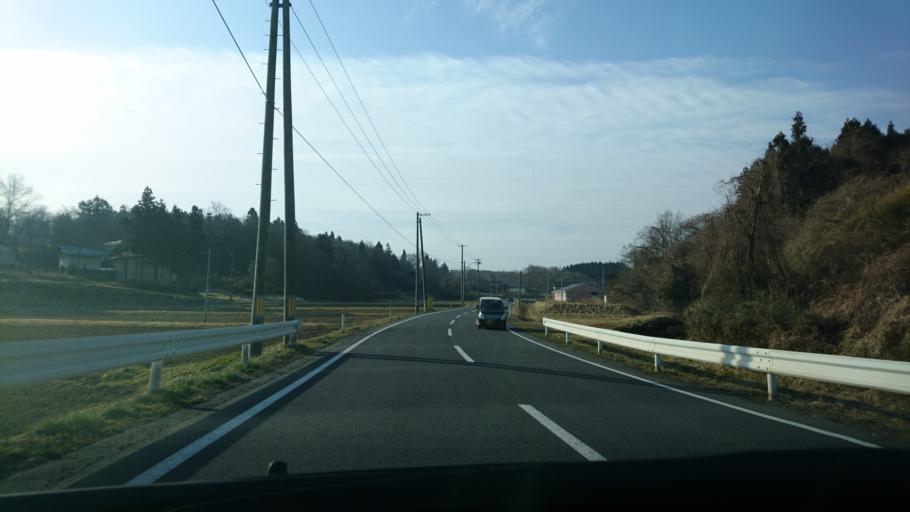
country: JP
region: Iwate
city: Ichinoseki
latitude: 38.8989
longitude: 141.1588
